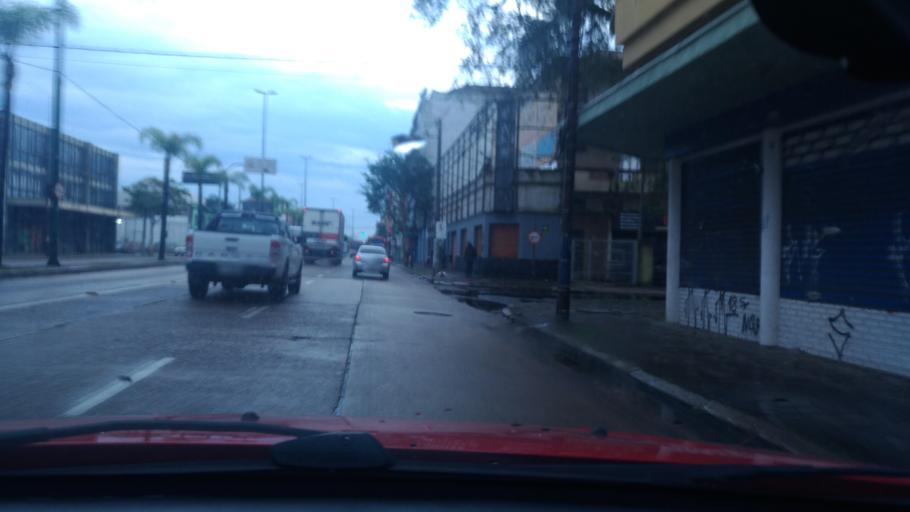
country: BR
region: Rio Grande do Sul
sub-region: Porto Alegre
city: Porto Alegre
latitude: -30.0092
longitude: -51.2021
